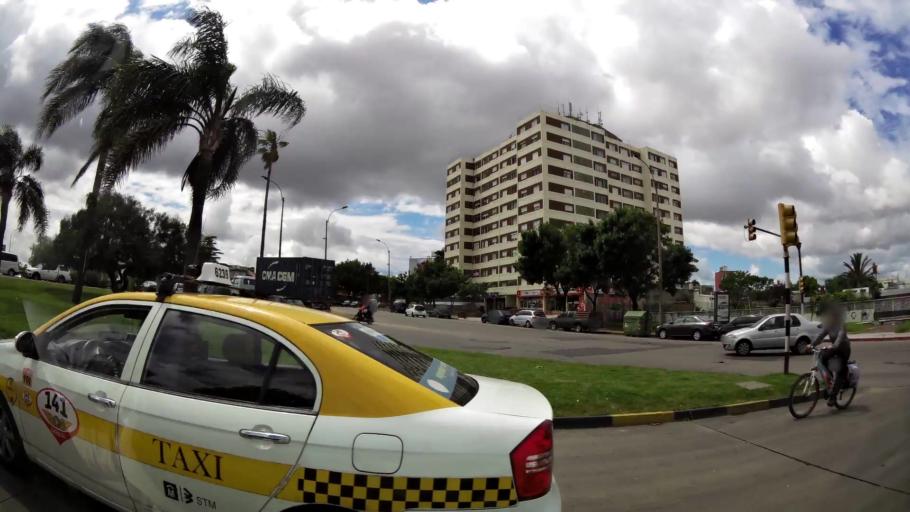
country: UY
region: Montevideo
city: Montevideo
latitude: -34.8697
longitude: -56.1673
